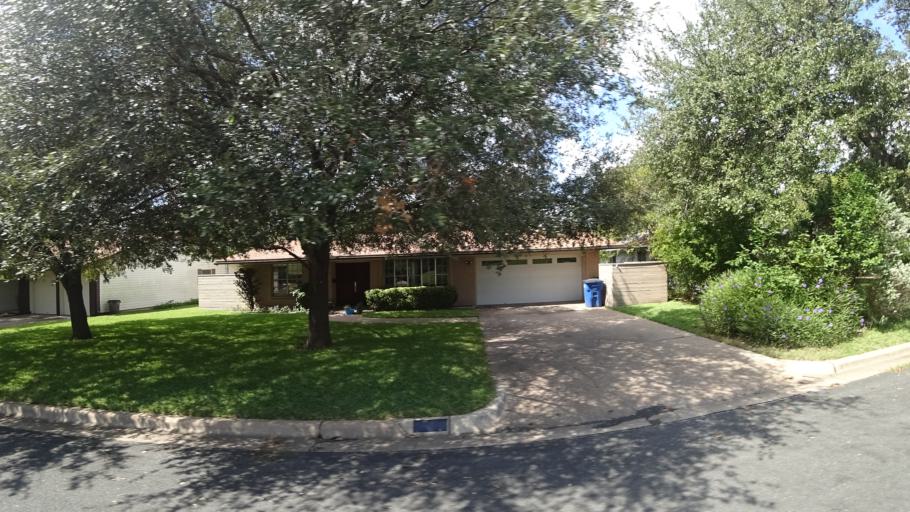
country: US
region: Texas
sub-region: Travis County
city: Austin
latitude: 30.3551
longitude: -97.7227
